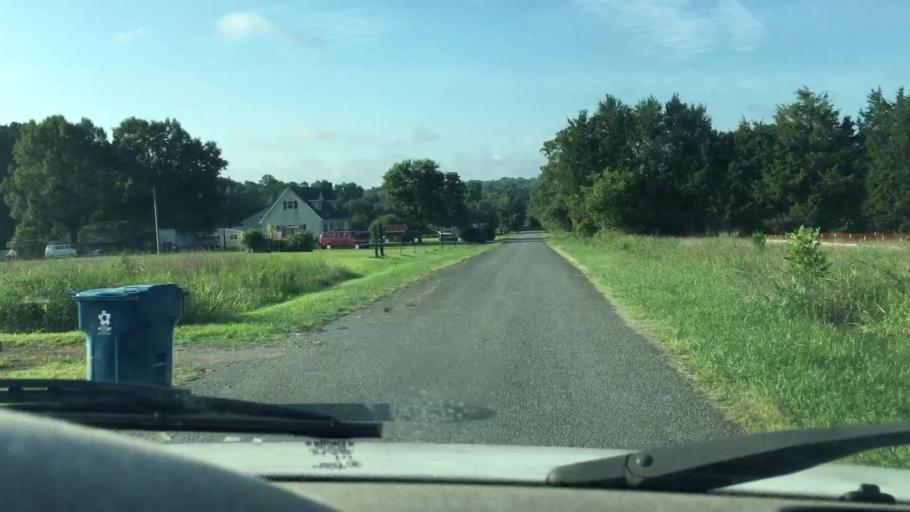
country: US
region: North Carolina
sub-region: Mecklenburg County
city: Huntersville
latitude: 35.4278
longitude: -80.8090
